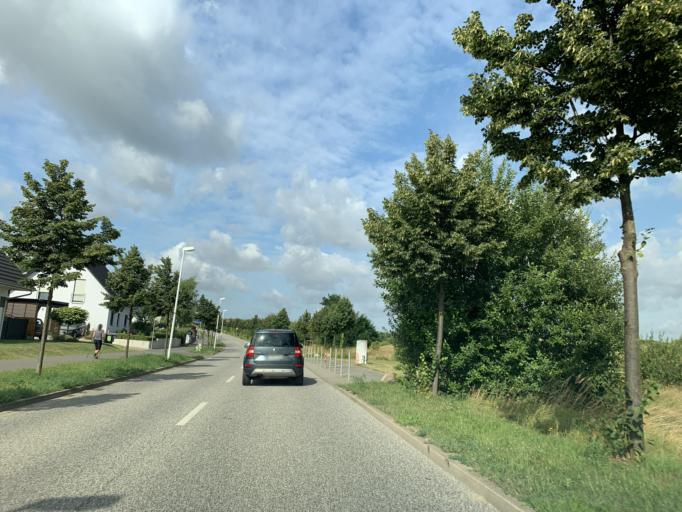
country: DE
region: Mecklenburg-Vorpommern
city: Neubrandenburg
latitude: 53.5291
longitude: 13.2752
